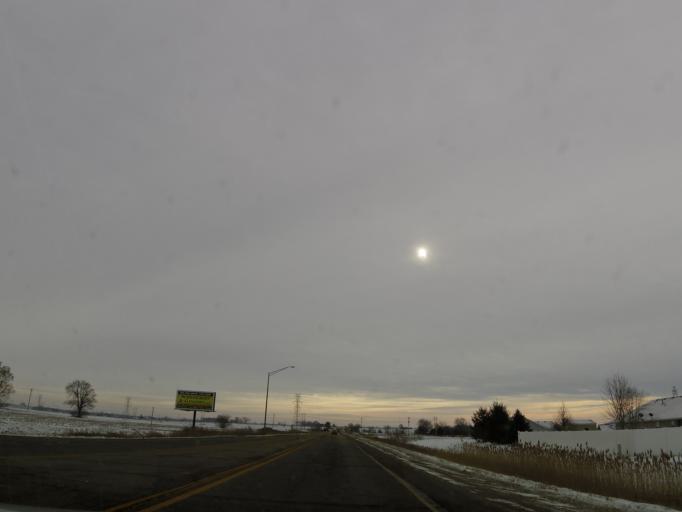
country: US
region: Illinois
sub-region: LaSalle County
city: La Salle
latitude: 41.2942
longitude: -89.1000
